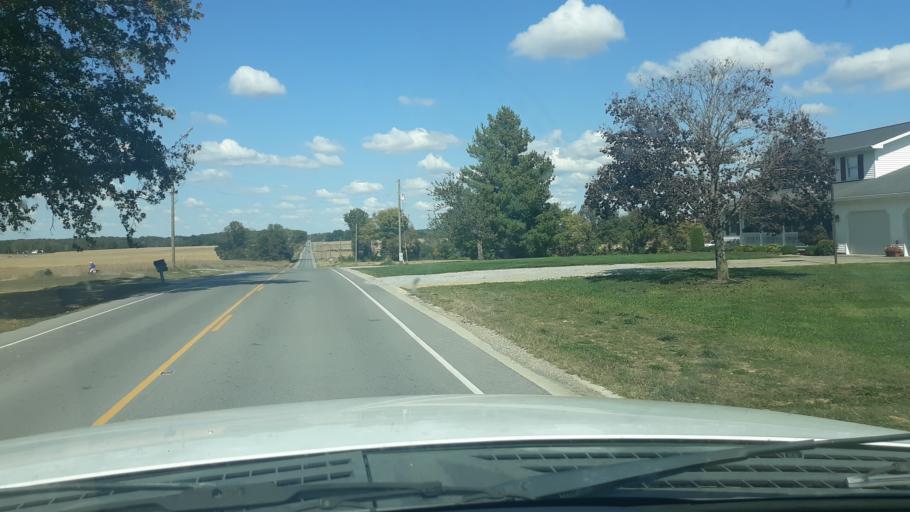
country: US
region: Illinois
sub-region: Saline County
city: Eldorado
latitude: 37.7948
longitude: -88.4848
